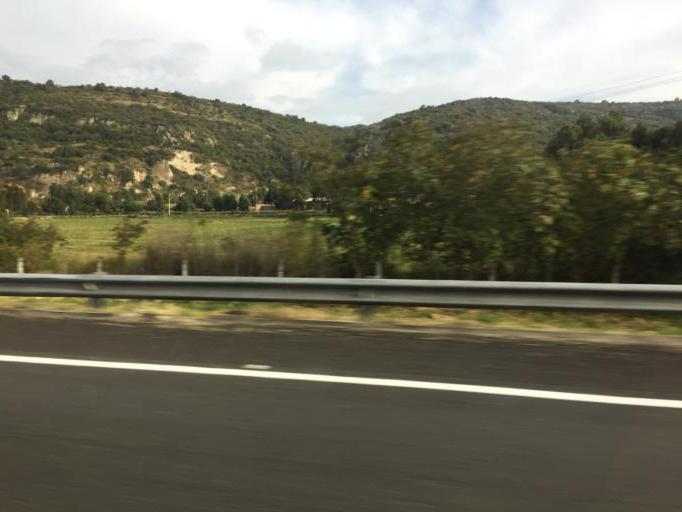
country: MX
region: Michoacan
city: Copandaro de Galeana
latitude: 19.8837
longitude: -101.1941
